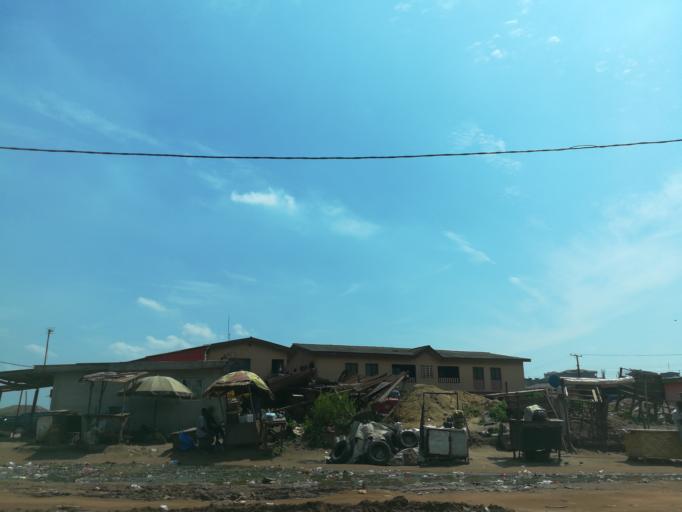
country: NG
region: Lagos
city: Ikorodu
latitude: 6.6571
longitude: 3.4758
